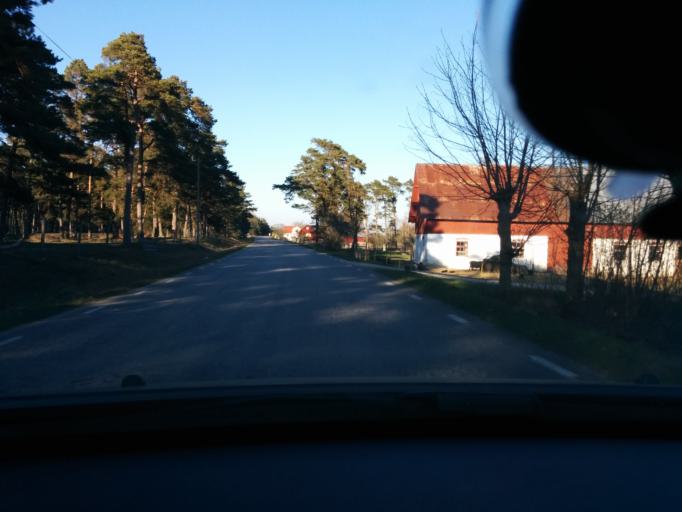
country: SE
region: Gotland
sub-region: Gotland
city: Hemse
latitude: 57.1862
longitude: 18.4157
